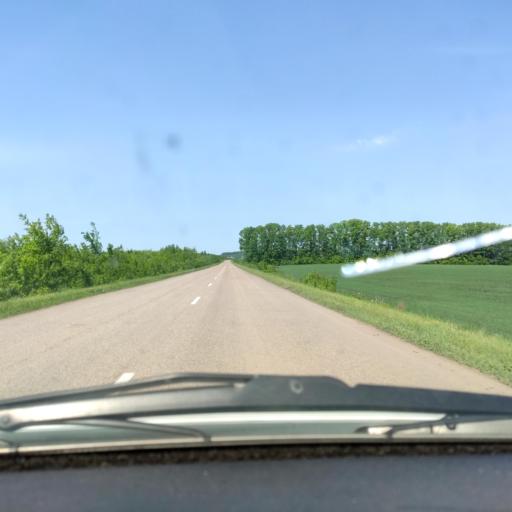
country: RU
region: Bashkortostan
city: Avdon
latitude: 54.5347
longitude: 55.6429
